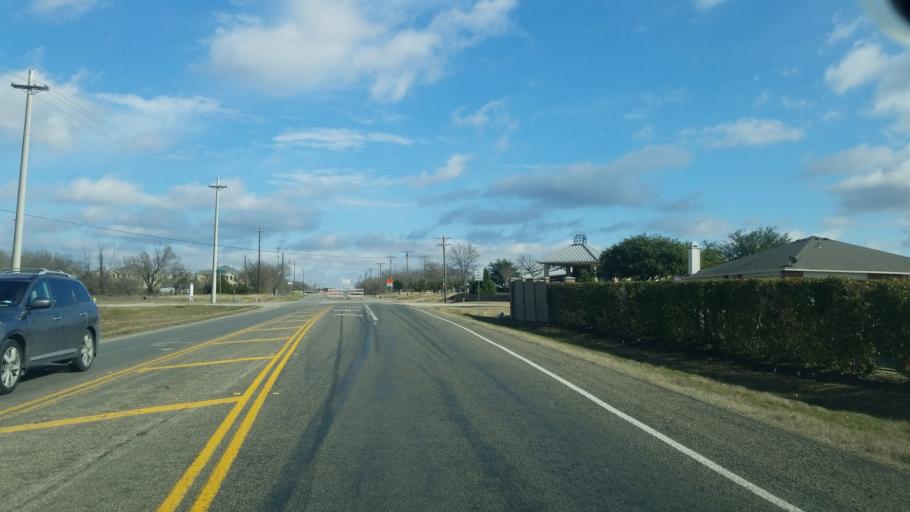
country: US
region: Texas
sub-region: Rockwall County
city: Rockwall
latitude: 32.9067
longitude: -96.4393
